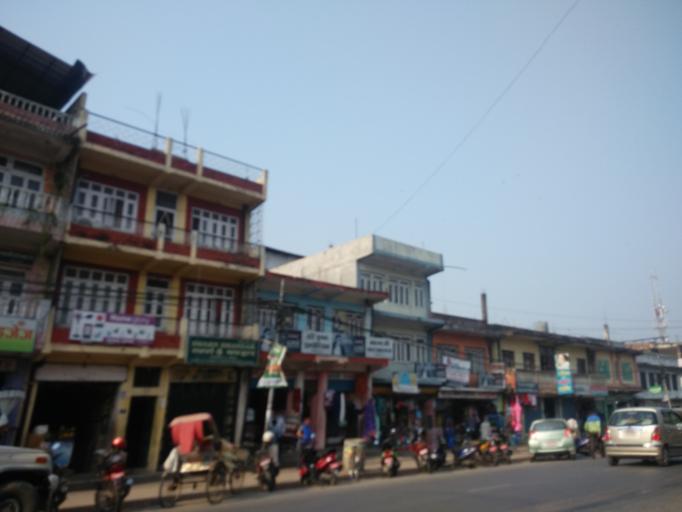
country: NP
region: Central Region
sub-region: Narayani Zone
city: Hitura
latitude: 27.4315
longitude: 85.0304
